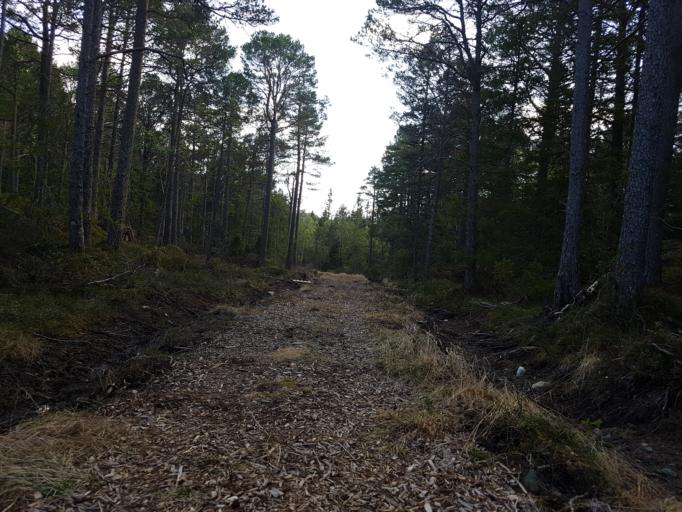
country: NO
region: Sor-Trondelag
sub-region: Trondheim
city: Trondheim
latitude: 63.4469
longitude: 10.2947
